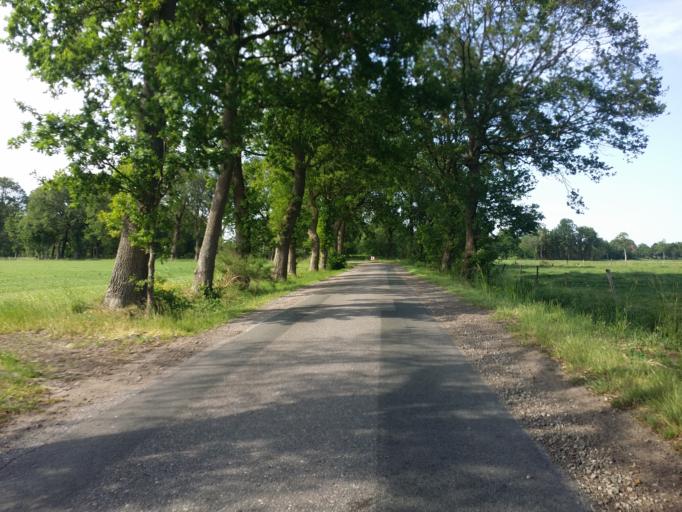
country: DE
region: Lower Saxony
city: Wiefelstede
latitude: 53.3139
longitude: 8.0520
